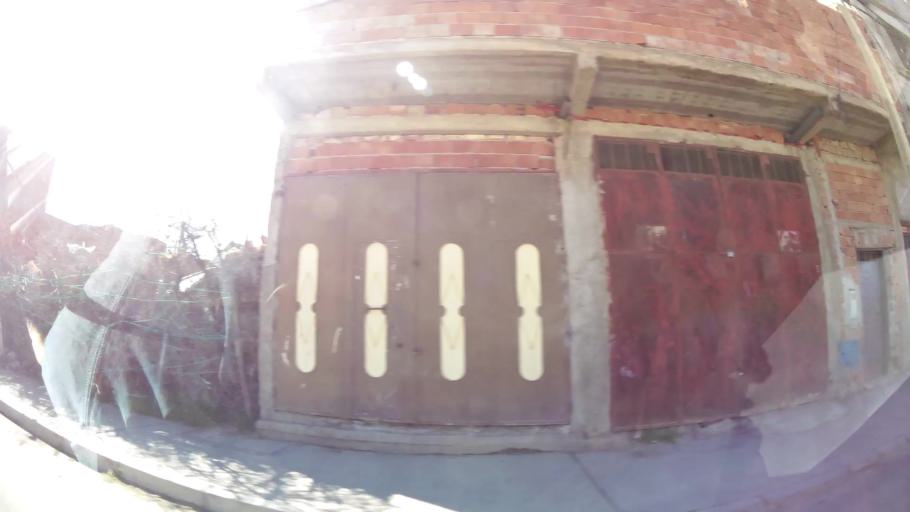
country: MA
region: Oriental
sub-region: Oujda-Angad
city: Oujda
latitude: 34.6462
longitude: -1.9492
